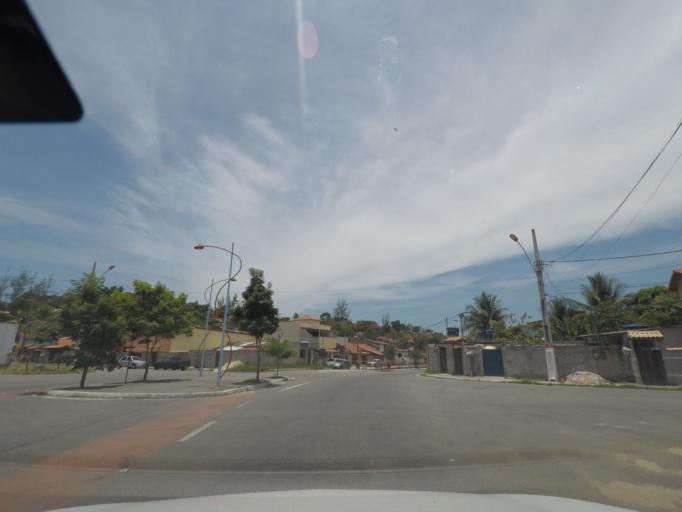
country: BR
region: Rio de Janeiro
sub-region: Marica
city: Marica
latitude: -22.9243
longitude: -42.8202
